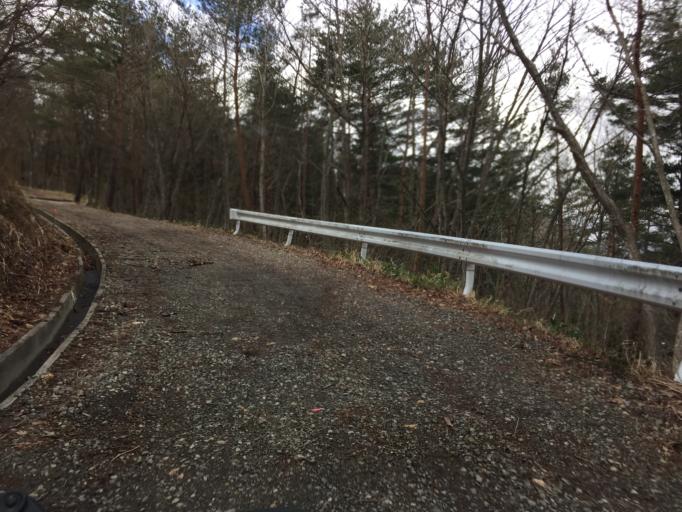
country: JP
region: Fukushima
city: Fukushima-shi
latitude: 37.8596
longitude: 140.4208
